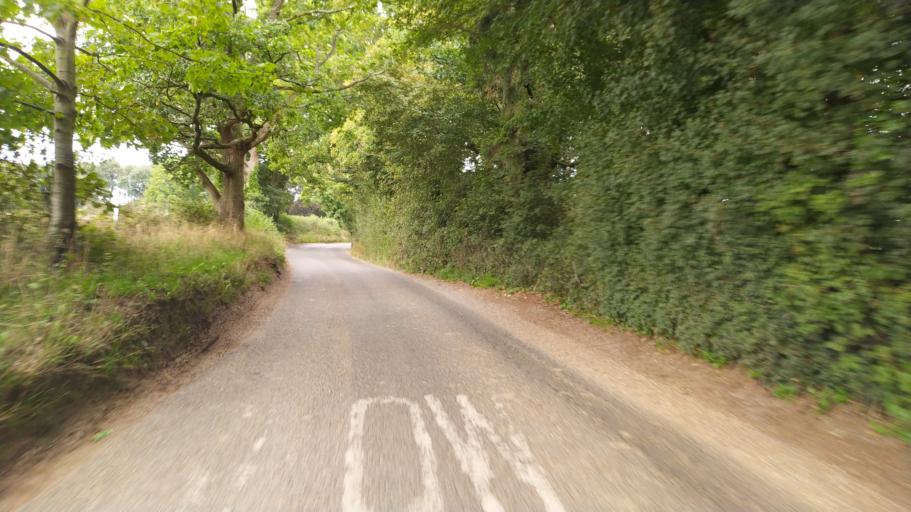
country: GB
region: England
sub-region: Hampshire
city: Romsey
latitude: 51.0043
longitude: -1.5167
